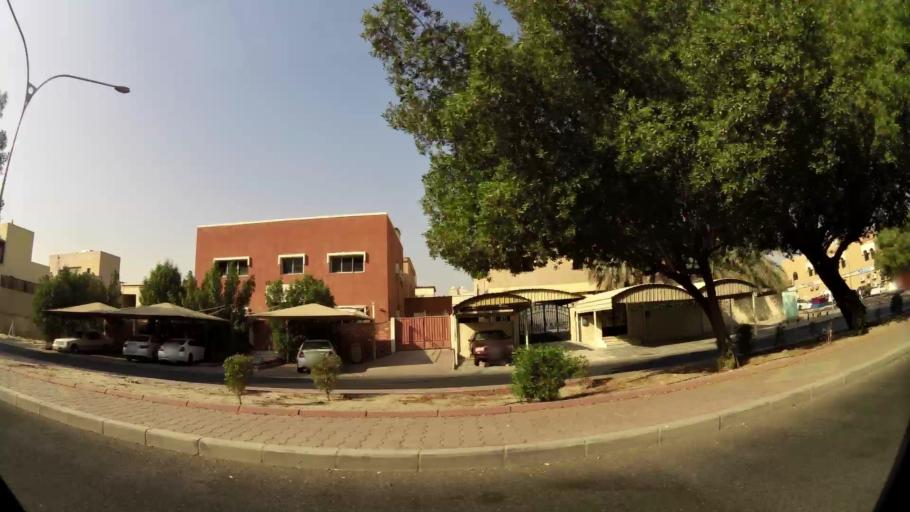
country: KW
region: Muhafazat Hawalli
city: Hawalli
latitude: 29.3237
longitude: 48.0380
